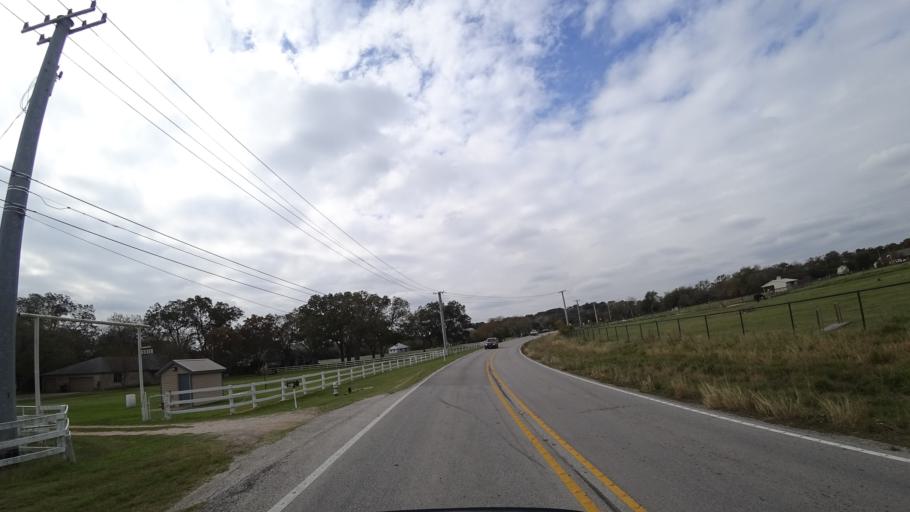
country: US
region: Texas
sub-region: Travis County
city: Shady Hollow
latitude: 30.2097
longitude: -97.9002
